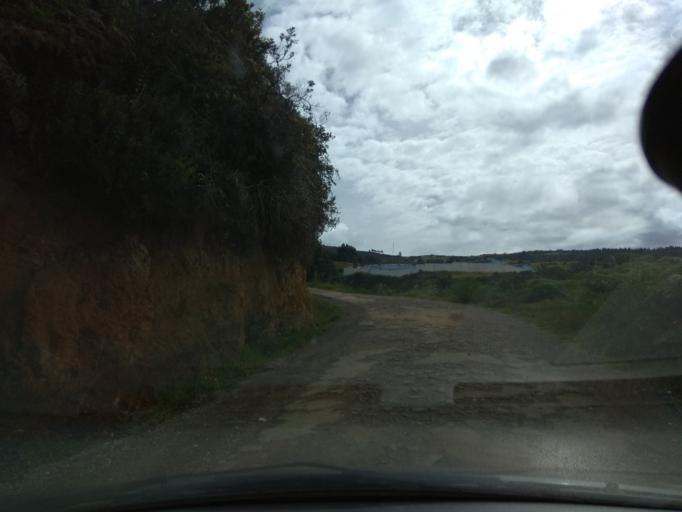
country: CO
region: Boyaca
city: Santa Rosa de Viterbo
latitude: 5.8913
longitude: -72.9728
